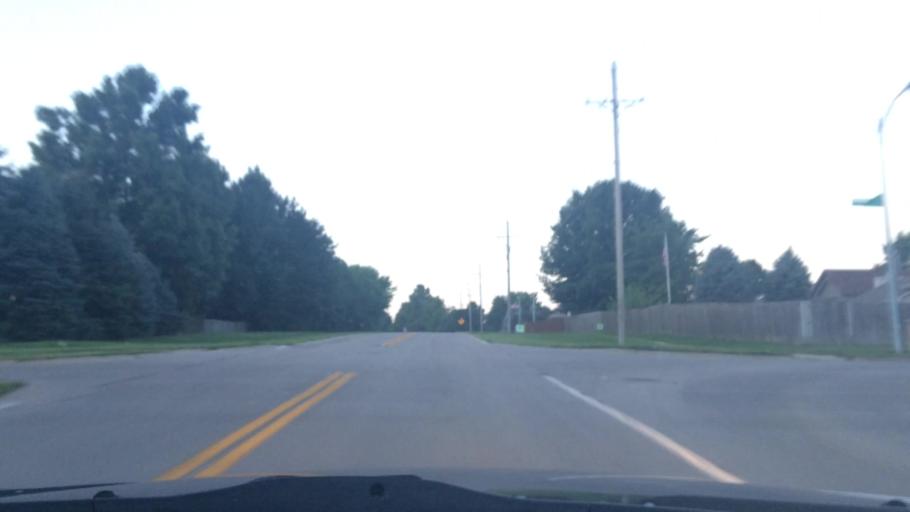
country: US
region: Nebraska
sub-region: Douglas County
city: Ralston
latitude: 41.1938
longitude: -96.0524
